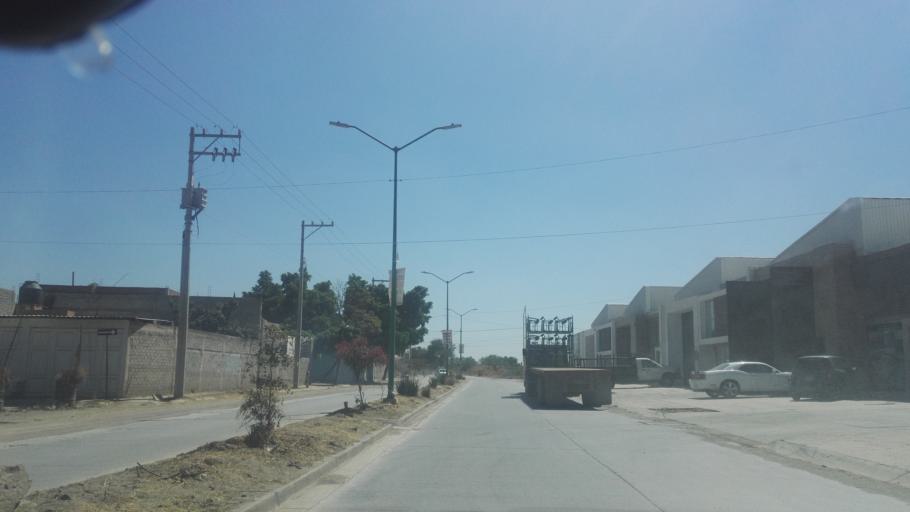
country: MX
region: Guanajuato
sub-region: Leon
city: Fraccionamiento Paraiso Real
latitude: 21.0889
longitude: -101.5937
